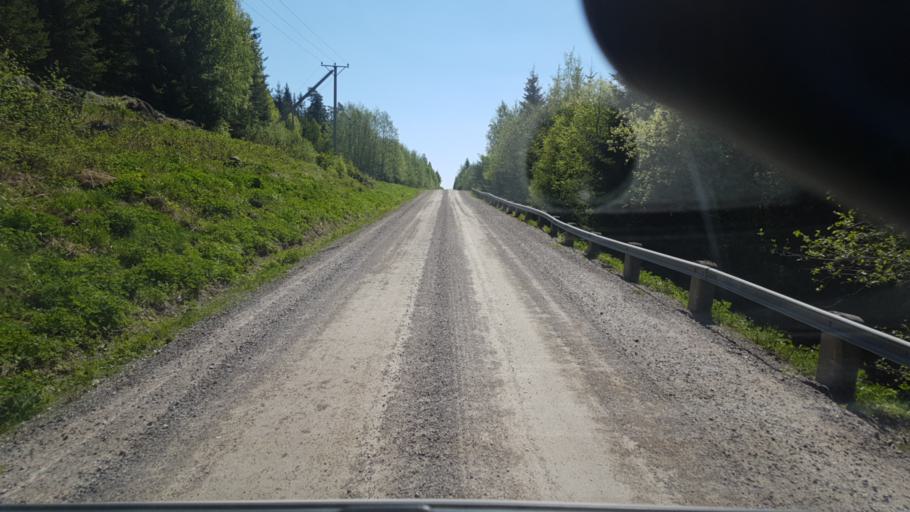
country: SE
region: Vaermland
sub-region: Arvika Kommun
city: Arvika
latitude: 59.8527
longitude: 12.7177
